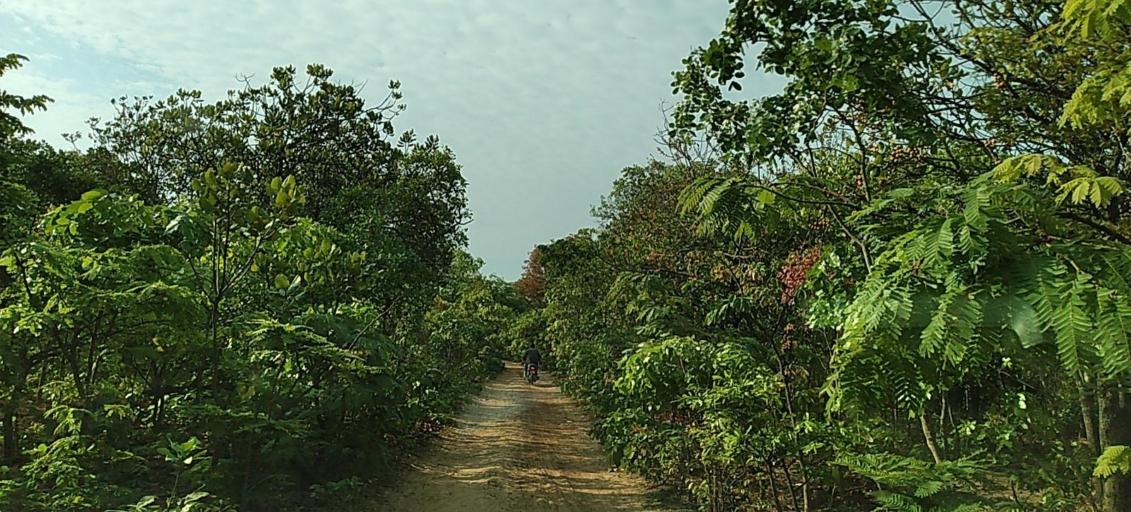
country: ZM
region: Copperbelt
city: Kalulushi
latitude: -12.9541
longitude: 27.6936
